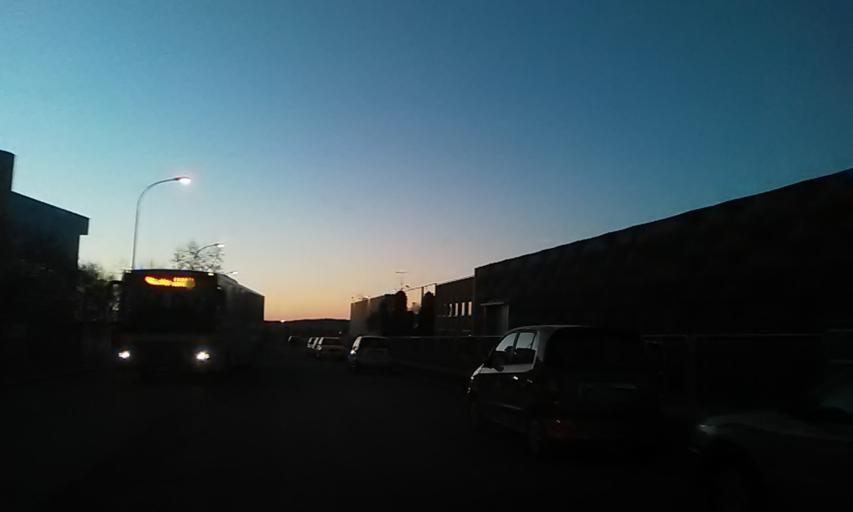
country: IT
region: Piedmont
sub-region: Provincia di Biella
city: Occhieppo Inferiore
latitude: 45.5547
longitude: 8.0316
